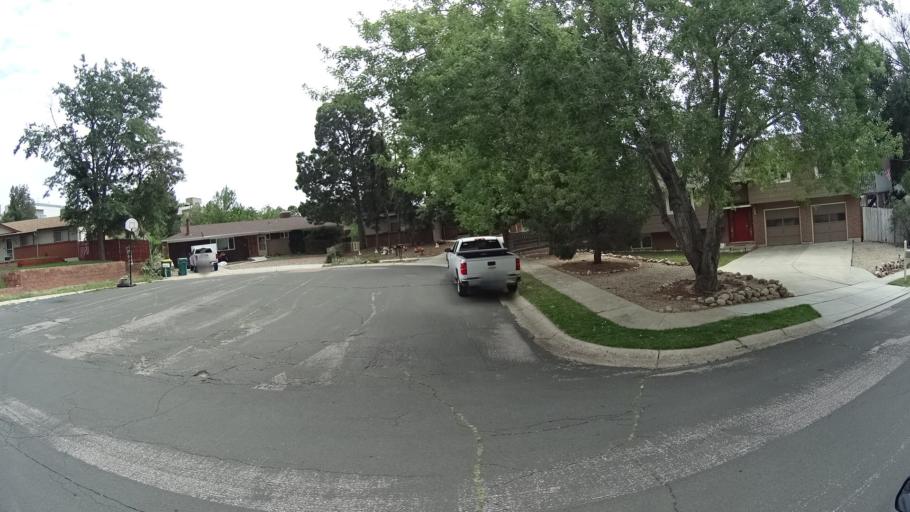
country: US
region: Colorado
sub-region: El Paso County
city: Colorado Springs
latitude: 38.8934
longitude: -104.8091
